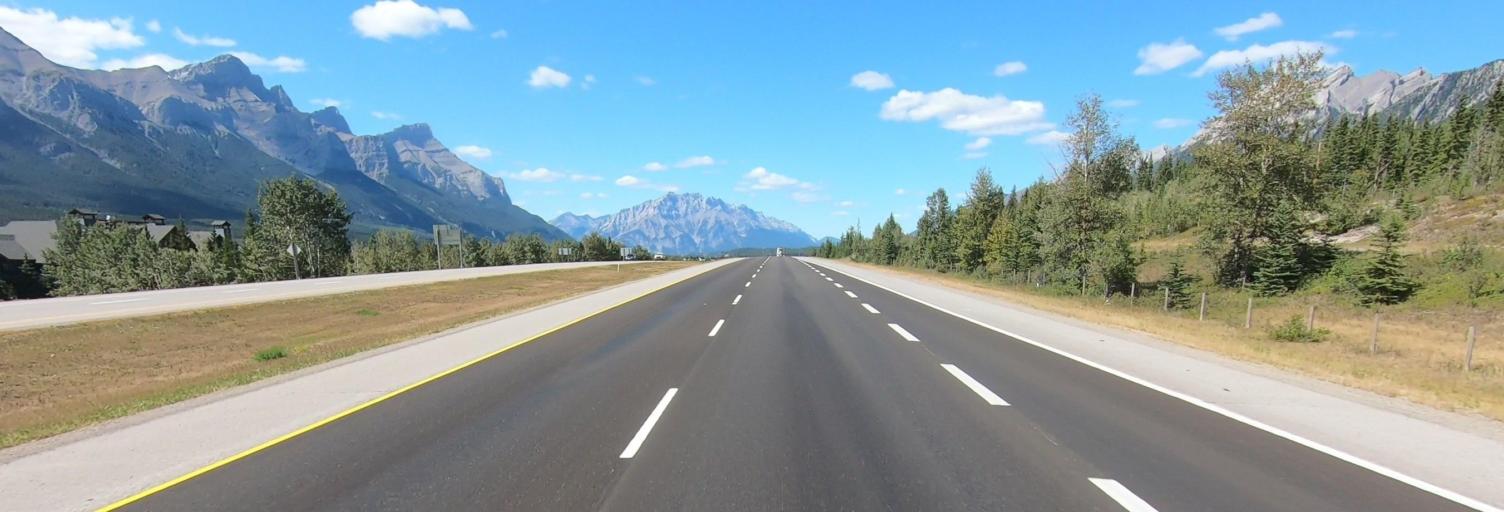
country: CA
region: Alberta
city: Canmore
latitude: 51.1003
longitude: -115.3562
